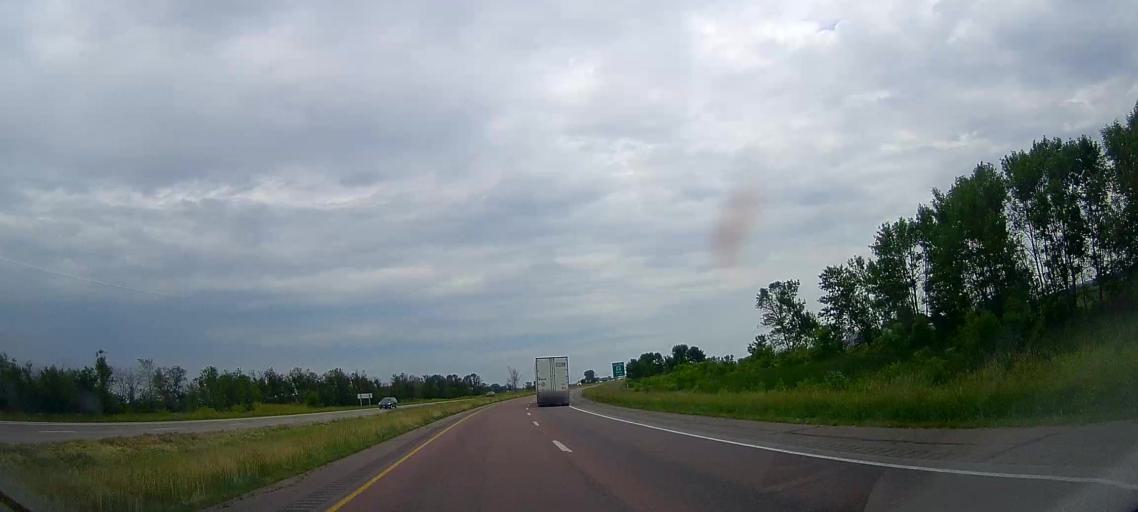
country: US
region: Iowa
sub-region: Woodbury County
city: Sergeant Bluff
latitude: 42.3207
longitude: -96.3083
